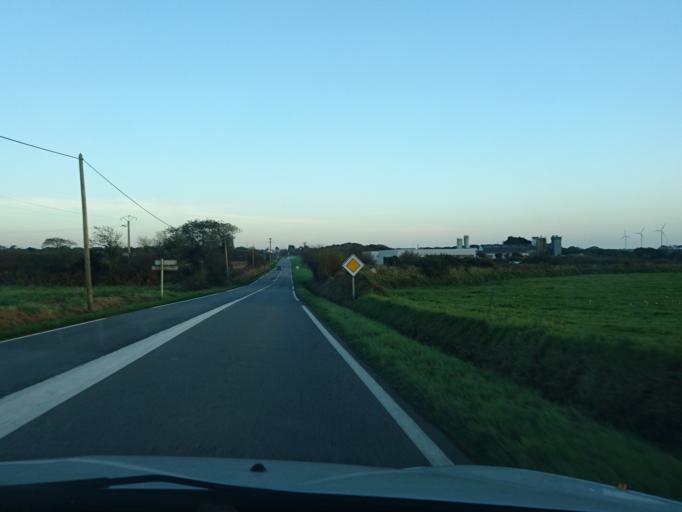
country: FR
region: Brittany
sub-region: Departement du Finistere
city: Lanrivoare
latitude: 48.4745
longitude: -4.6513
